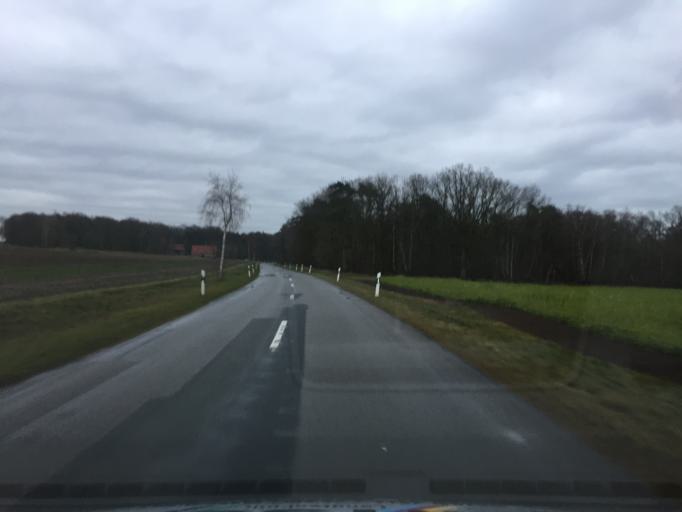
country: DE
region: Lower Saxony
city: Borstel
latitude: 52.6518
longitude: 8.9904
